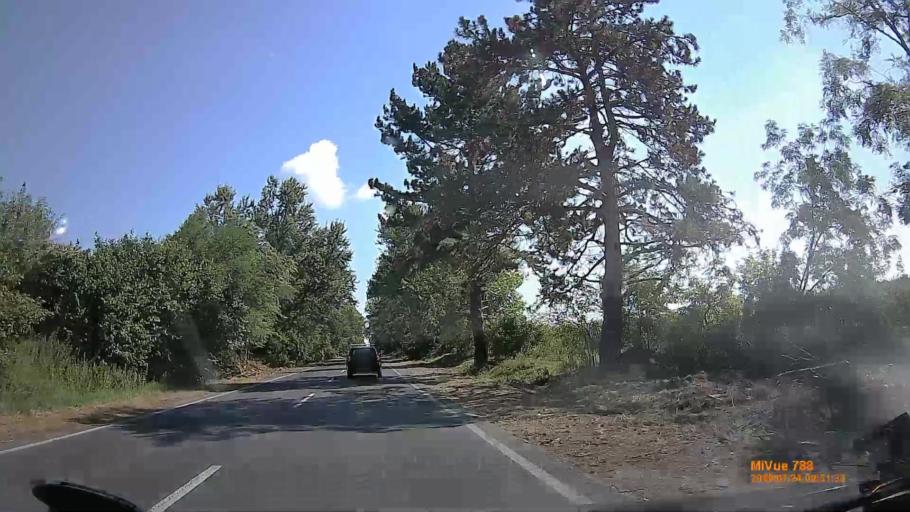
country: HU
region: Szabolcs-Szatmar-Bereg
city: Vaja
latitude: 48.0324
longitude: 22.1701
